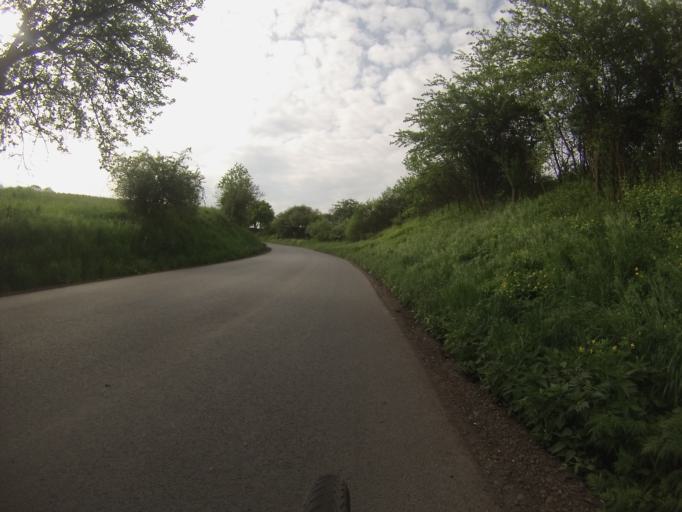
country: CZ
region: South Moravian
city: Cebin
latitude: 49.3077
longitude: 16.4615
